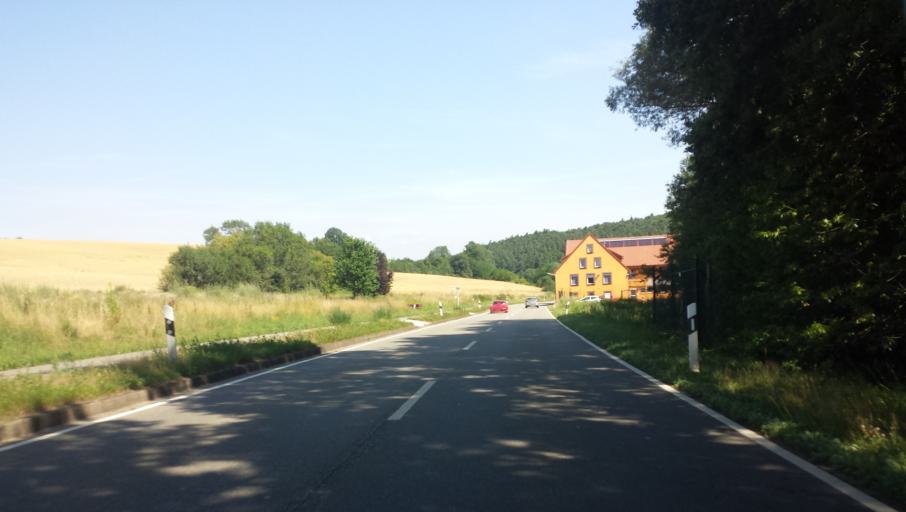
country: DE
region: Rheinland-Pfalz
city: Enkenbach-Alsenborn
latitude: 49.5006
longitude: 7.8929
